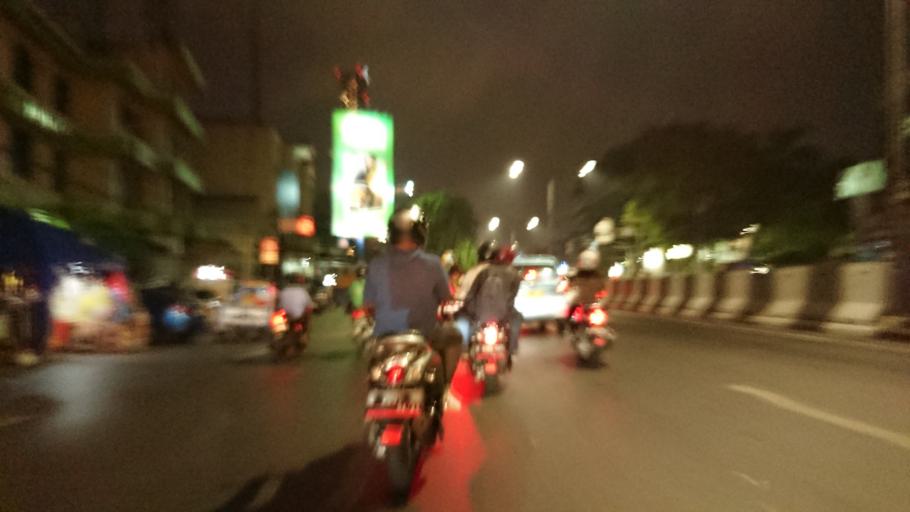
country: ID
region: Jakarta Raya
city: Jakarta
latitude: -6.1904
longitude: 106.8152
